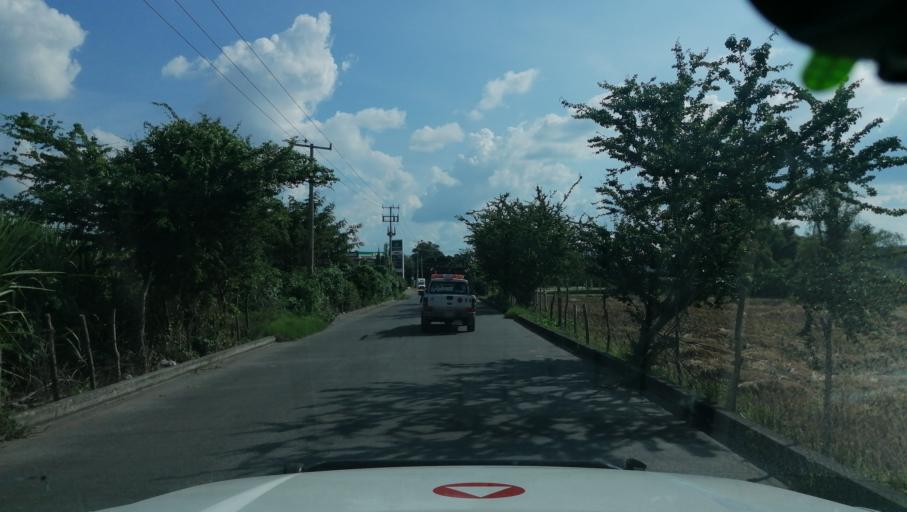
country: MX
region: Morelos
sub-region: Ayala
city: San Pedro Apatlaco
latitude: 18.8040
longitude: -98.9644
